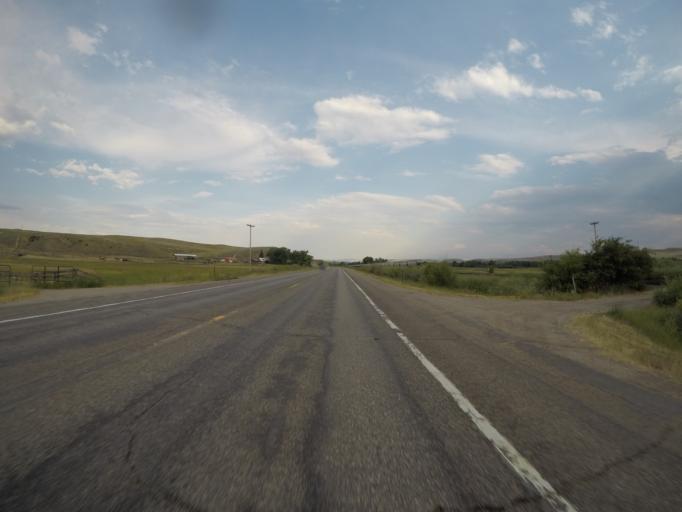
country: US
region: Colorado
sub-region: Routt County
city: Hayden
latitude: 40.5136
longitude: -107.3902
